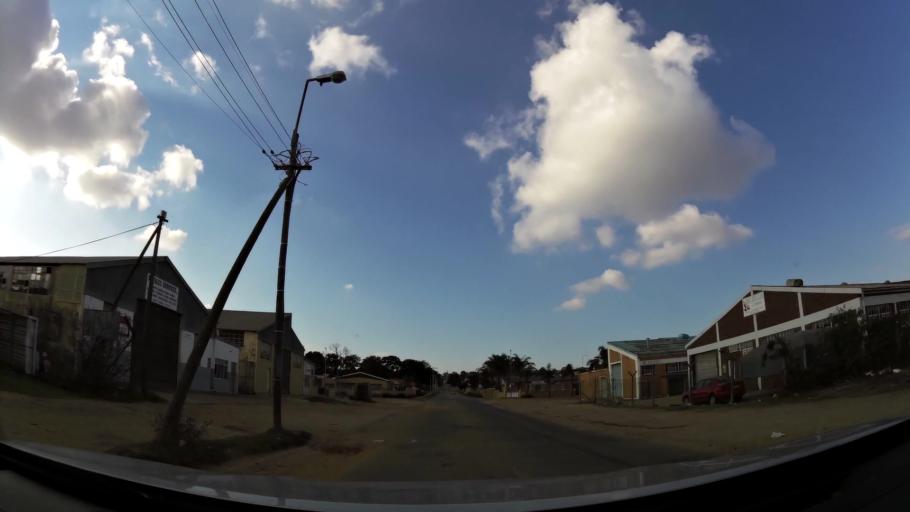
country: ZA
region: Eastern Cape
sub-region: Nelson Mandela Bay Metropolitan Municipality
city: Uitenhage
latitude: -33.7724
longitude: 25.3931
